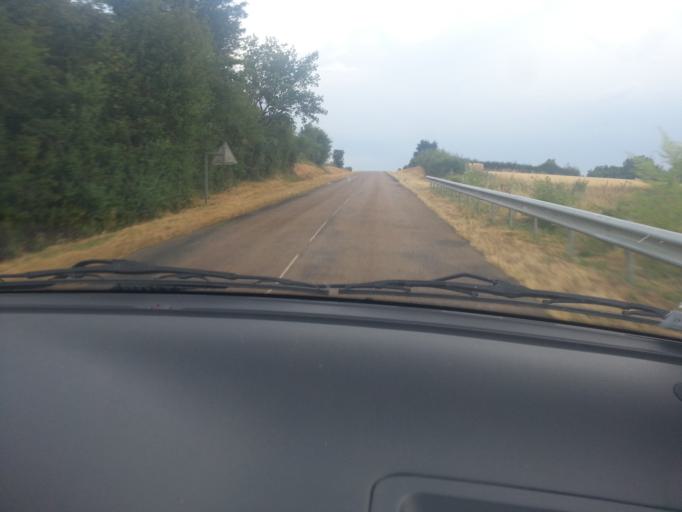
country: FR
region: Bourgogne
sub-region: Departement de Saone-et-Loire
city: Buxy
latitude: 46.7422
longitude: 4.6430
